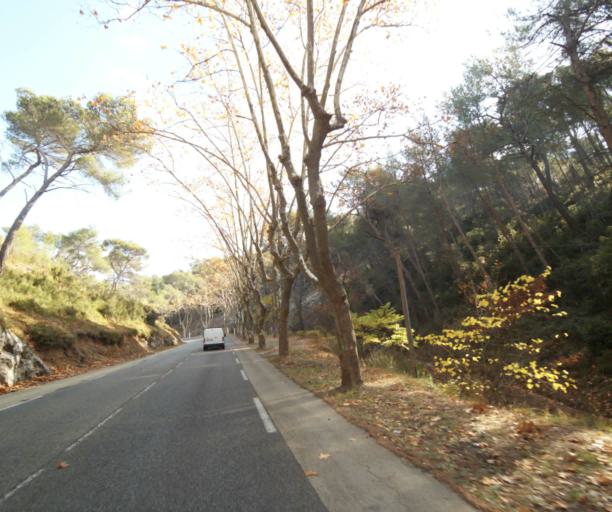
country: FR
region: Provence-Alpes-Cote d'Azur
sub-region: Departement des Bouches-du-Rhone
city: Allauch
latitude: 43.3706
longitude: 5.5059
